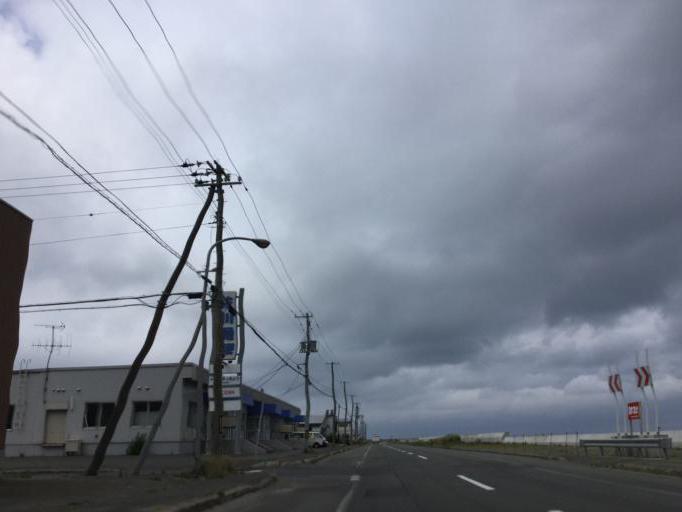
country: JP
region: Hokkaido
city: Wakkanai
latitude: 45.3971
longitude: 141.7064
